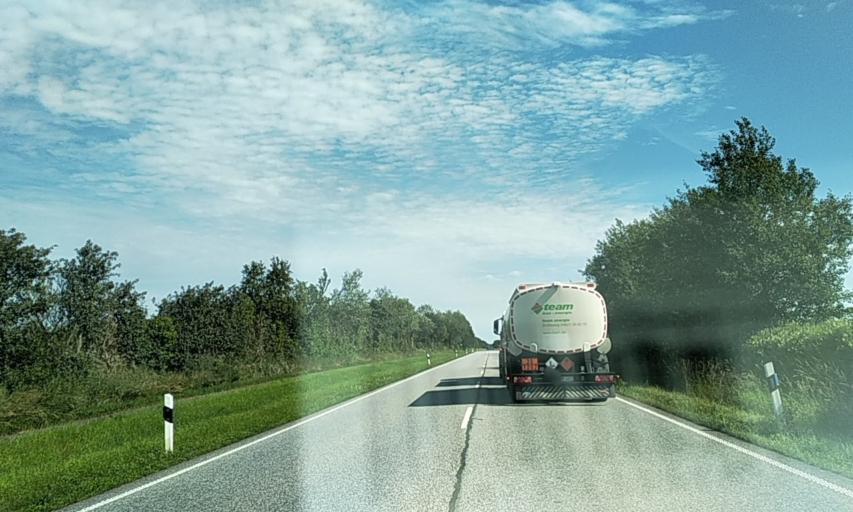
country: DE
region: Schleswig-Holstein
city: Kropp
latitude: 54.4254
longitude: 9.5312
